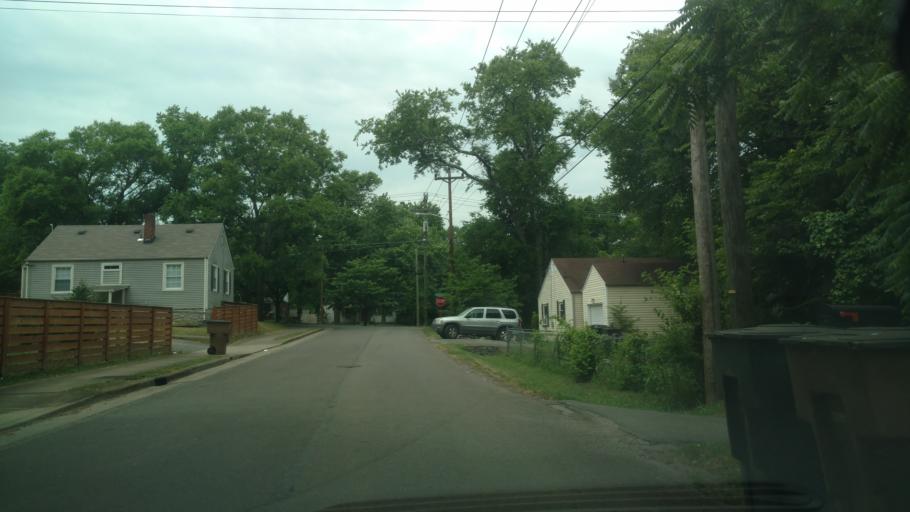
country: US
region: Tennessee
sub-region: Davidson County
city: Nashville
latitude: 36.2008
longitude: -86.7220
